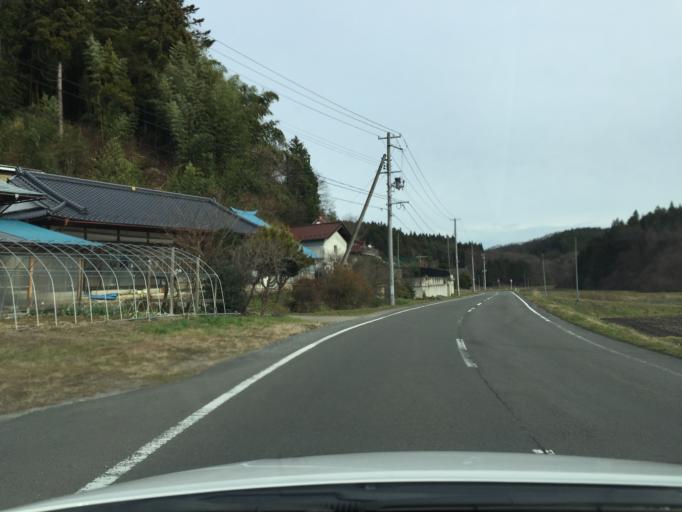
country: JP
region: Fukushima
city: Ishikawa
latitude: 37.2178
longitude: 140.6277
